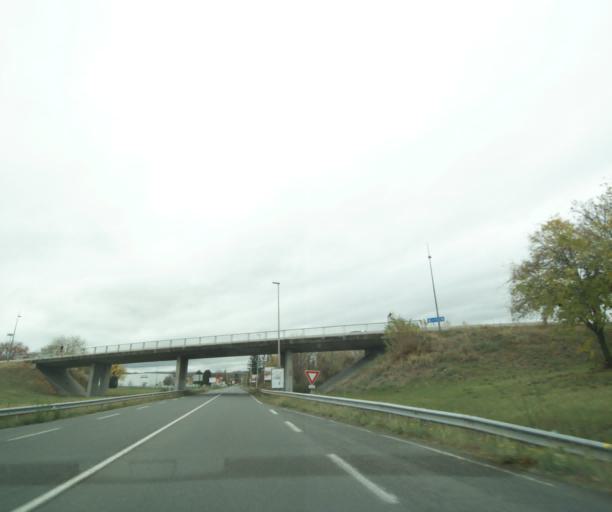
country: FR
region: Auvergne
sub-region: Departement du Puy-de-Dome
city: Dallet
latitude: 45.7793
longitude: 3.2031
